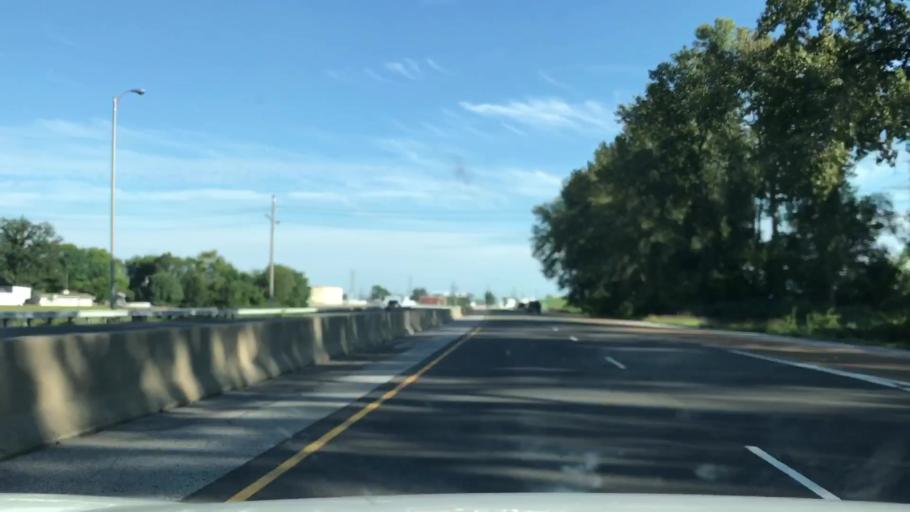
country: US
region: Illinois
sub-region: Madison County
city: Wood River
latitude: 38.8564
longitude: -90.1073
